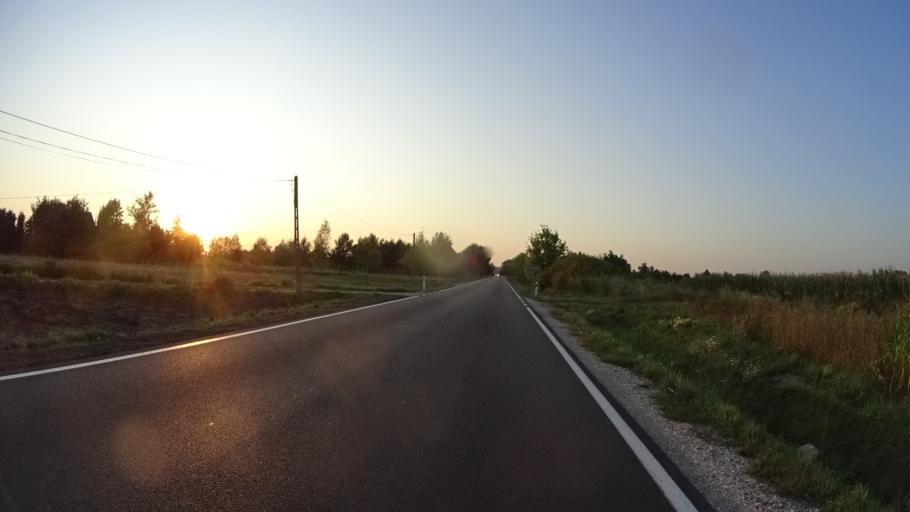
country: PL
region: Masovian Voivodeship
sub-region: Powiat warszawski zachodni
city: Ozarow Mazowiecki
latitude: 52.2478
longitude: 20.7440
